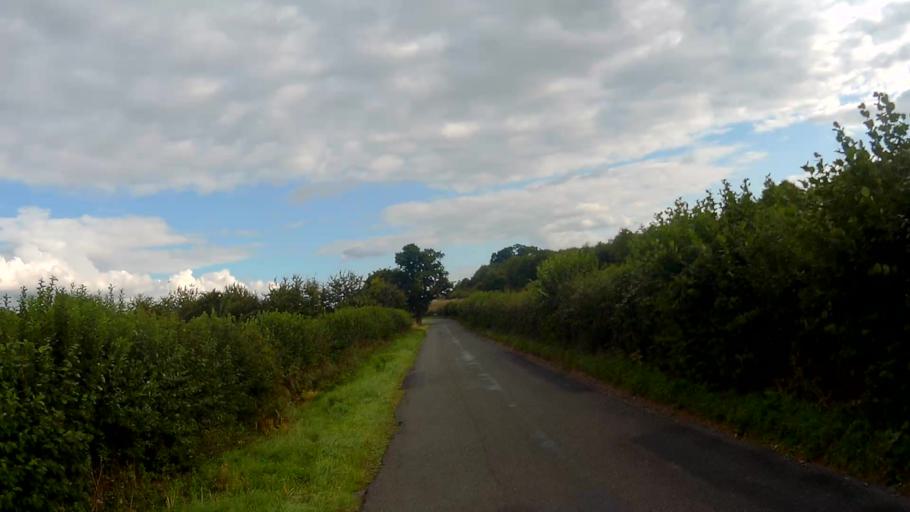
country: GB
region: England
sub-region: Hampshire
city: Kings Worthy
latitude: 51.1462
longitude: -1.2179
